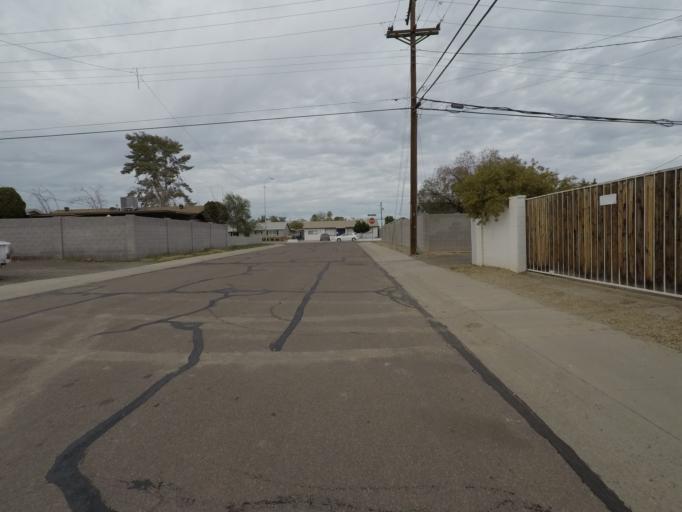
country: US
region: Arizona
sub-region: Maricopa County
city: Tempe Junction
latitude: 33.4543
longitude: -111.9316
